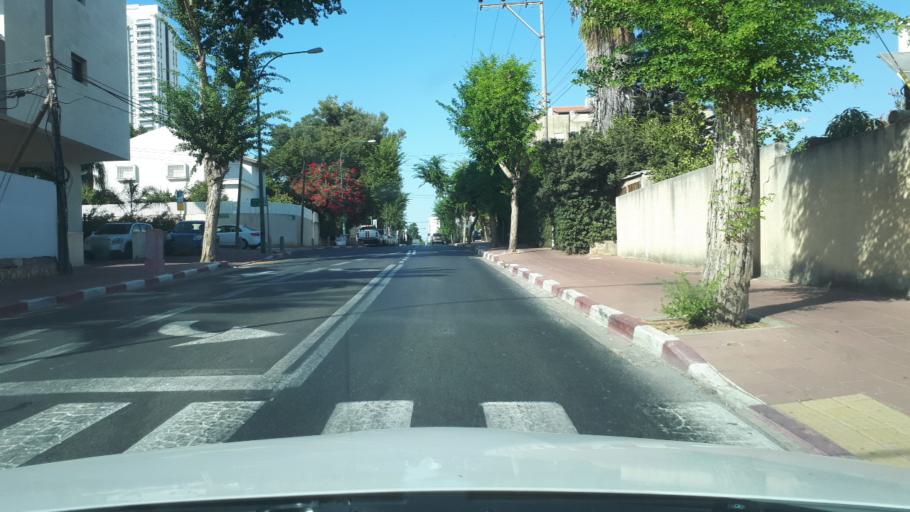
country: IL
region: Tel Aviv
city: Giv`atayim
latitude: 32.0668
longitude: 34.8241
